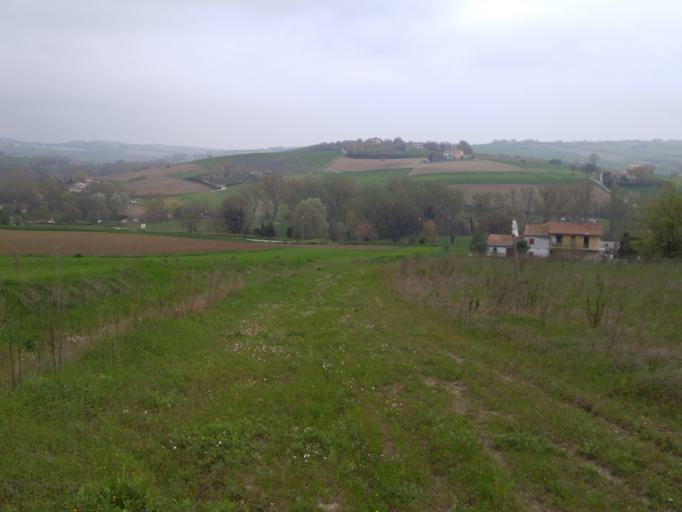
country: IT
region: The Marches
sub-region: Provincia di Pesaro e Urbino
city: Calcinelli
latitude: 43.7734
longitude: 12.9158
